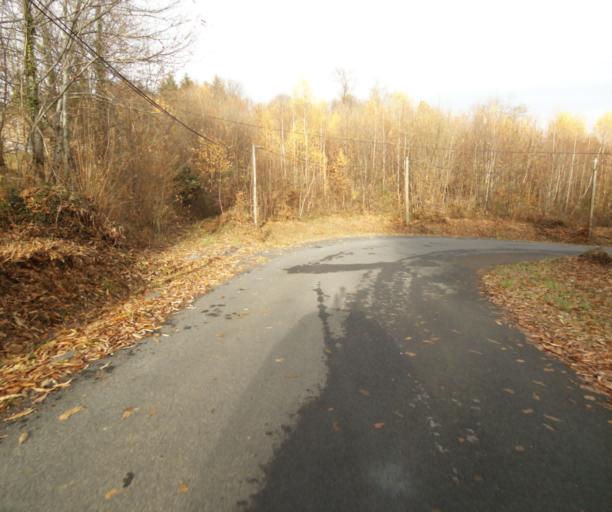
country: FR
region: Limousin
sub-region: Departement de la Correze
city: Sainte-Fortunade
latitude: 45.1921
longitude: 1.7840
